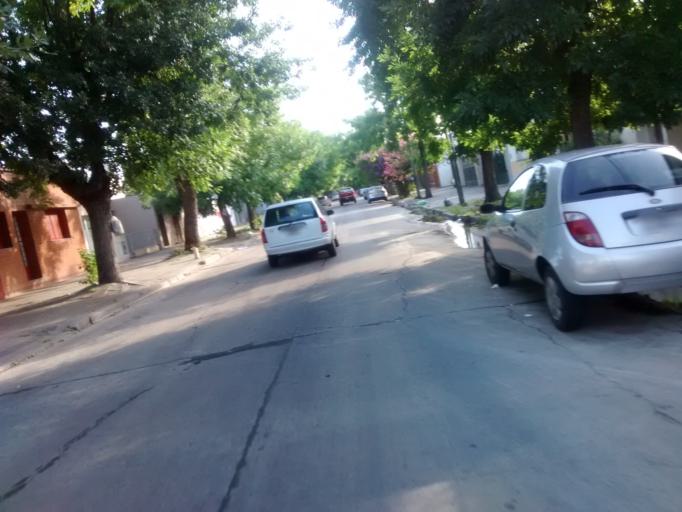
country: AR
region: Buenos Aires
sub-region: Partido de La Plata
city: La Plata
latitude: -34.9108
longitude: -57.9739
